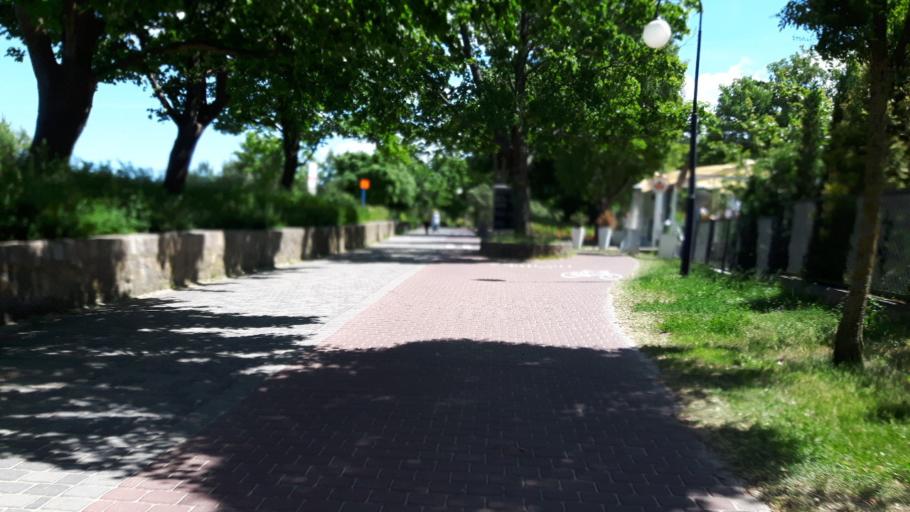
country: PL
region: Pomeranian Voivodeship
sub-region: Sopot
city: Sopot
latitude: 54.4365
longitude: 18.5807
